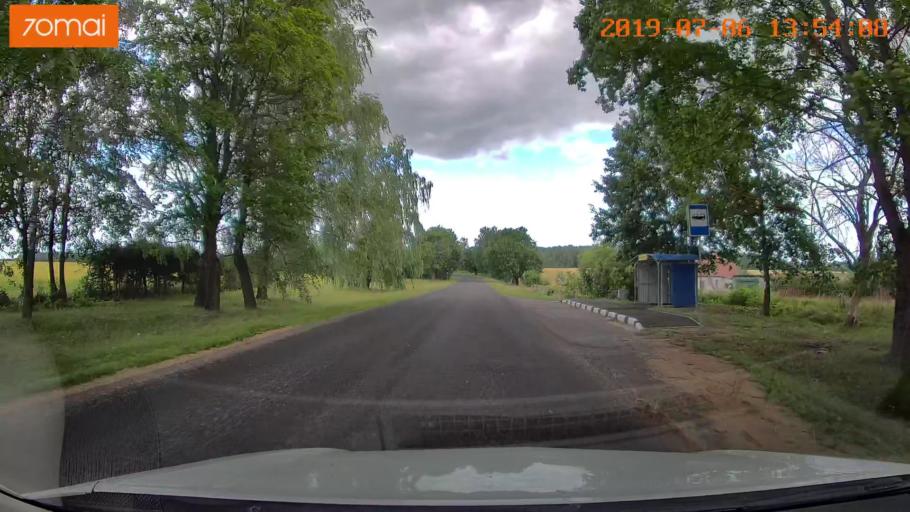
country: BY
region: Minsk
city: Ivyanyets
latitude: 53.7426
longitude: 26.8217
